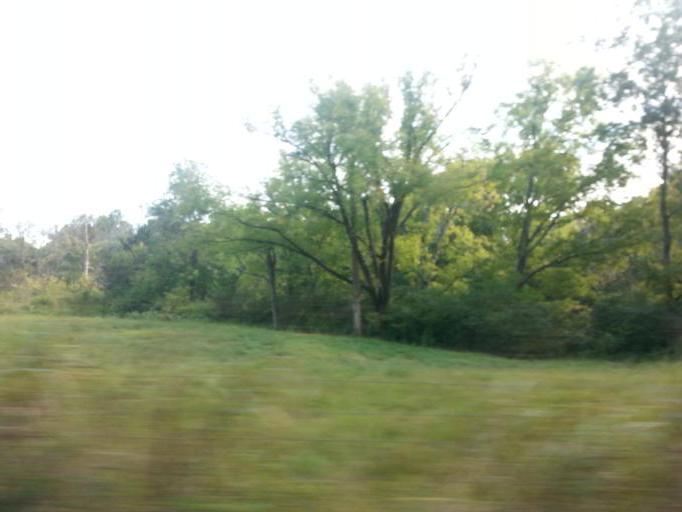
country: US
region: Tennessee
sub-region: Blount County
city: Eagleton Village
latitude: 35.8209
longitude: -83.9307
